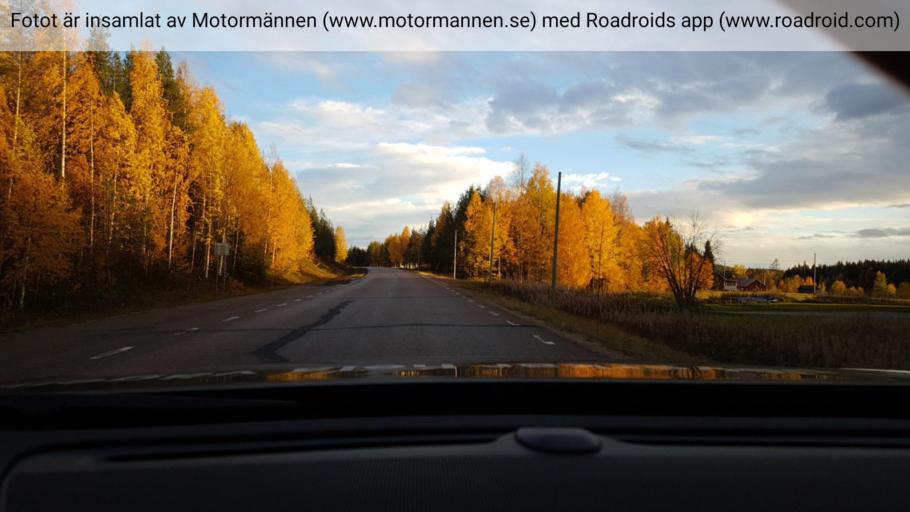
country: SE
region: Norrbotten
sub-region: Overkalix Kommun
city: OEverkalix
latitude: 66.6277
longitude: 22.7354
